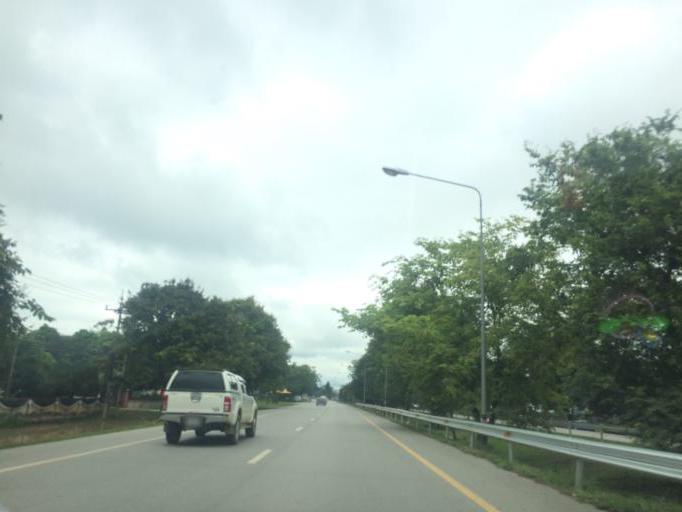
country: TH
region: Chiang Rai
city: Chiang Rai
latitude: 19.8558
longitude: 99.8152
